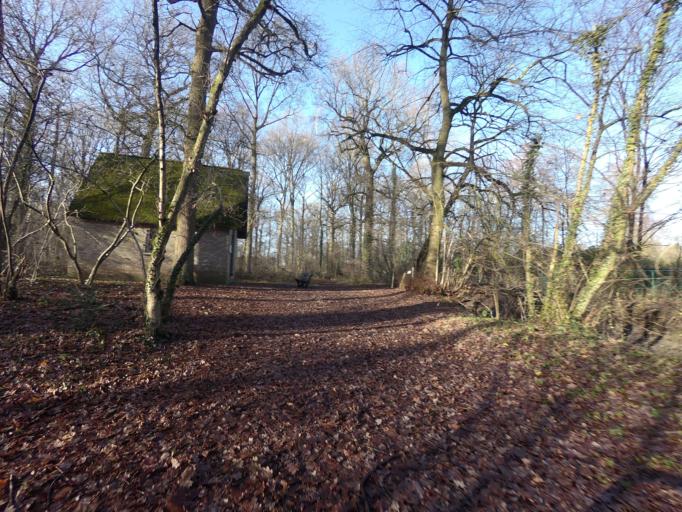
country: BE
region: Flanders
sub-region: Provincie Antwerpen
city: Lint
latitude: 51.1338
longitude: 4.5206
